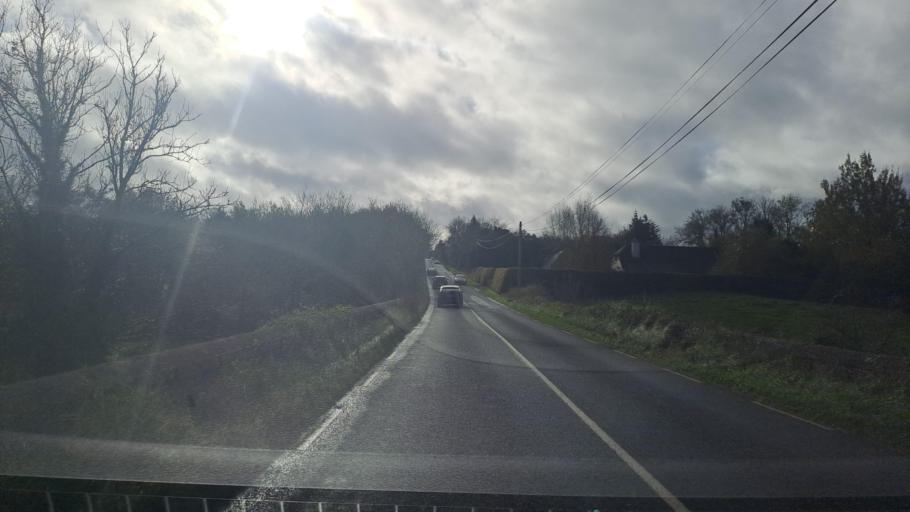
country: IE
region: Ulster
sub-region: County Monaghan
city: Monaghan
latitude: 54.1963
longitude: -6.9898
